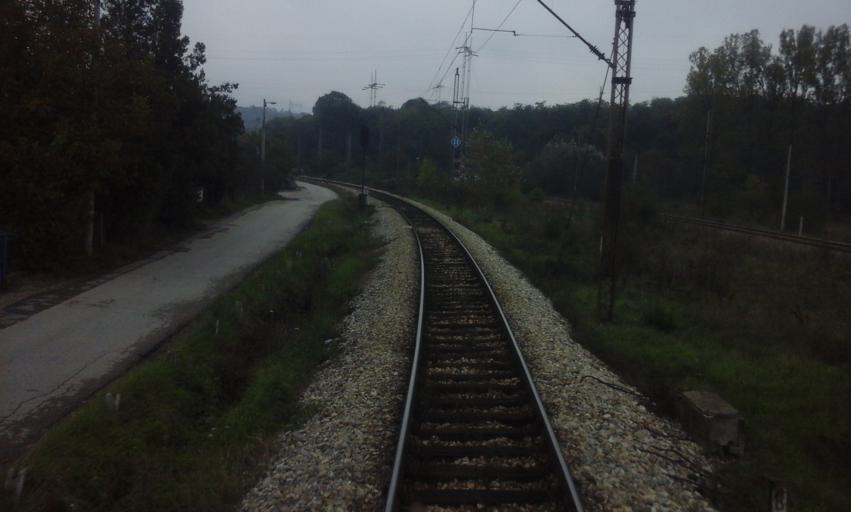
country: RS
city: Rusanj
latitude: 44.6996
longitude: 20.4534
